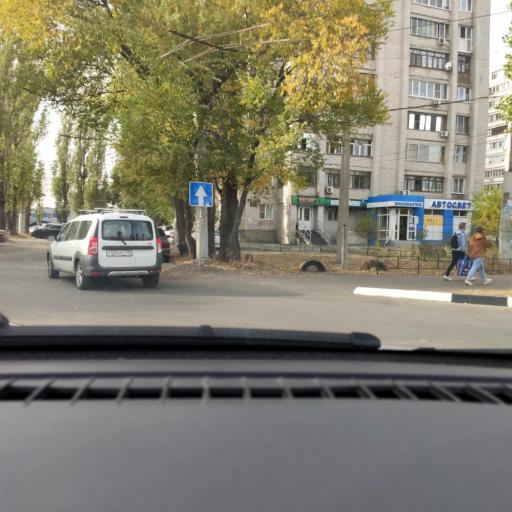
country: RU
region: Voronezj
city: Voronezh
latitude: 51.7011
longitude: 39.2742
